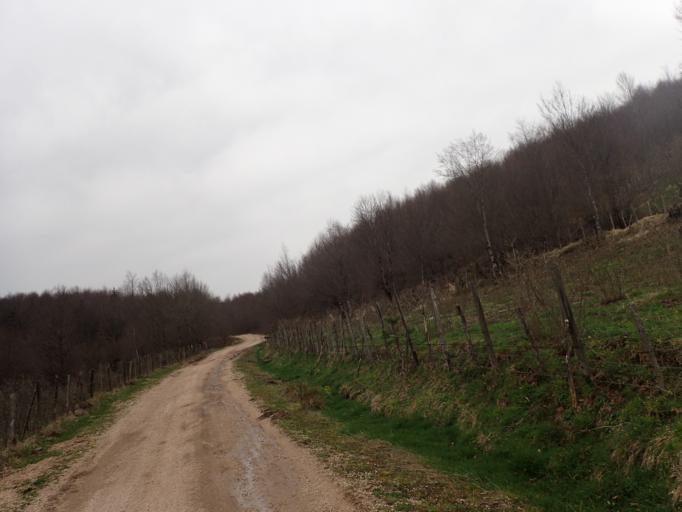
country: TR
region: Ordu
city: Kumru
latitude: 40.8037
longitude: 37.1645
